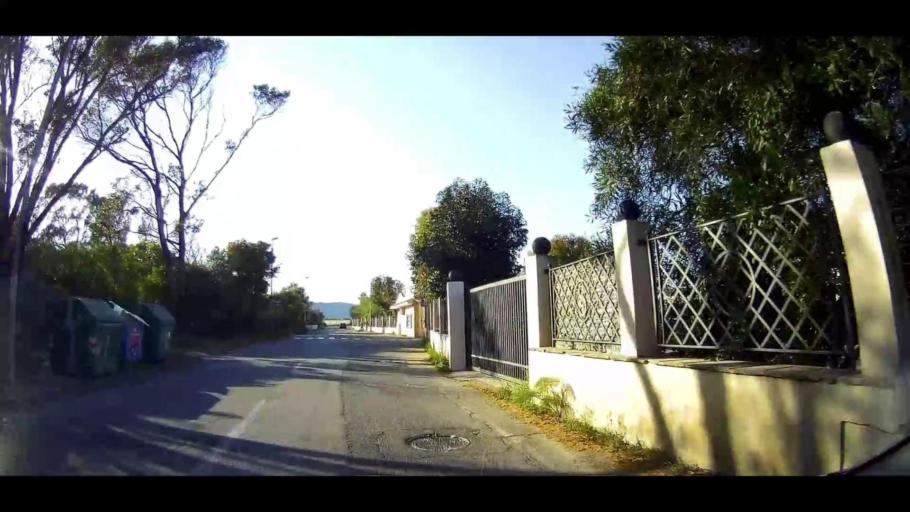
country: IT
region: Calabria
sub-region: Provincia di Crotone
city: Crotone
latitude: 39.0481
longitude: 17.1448
